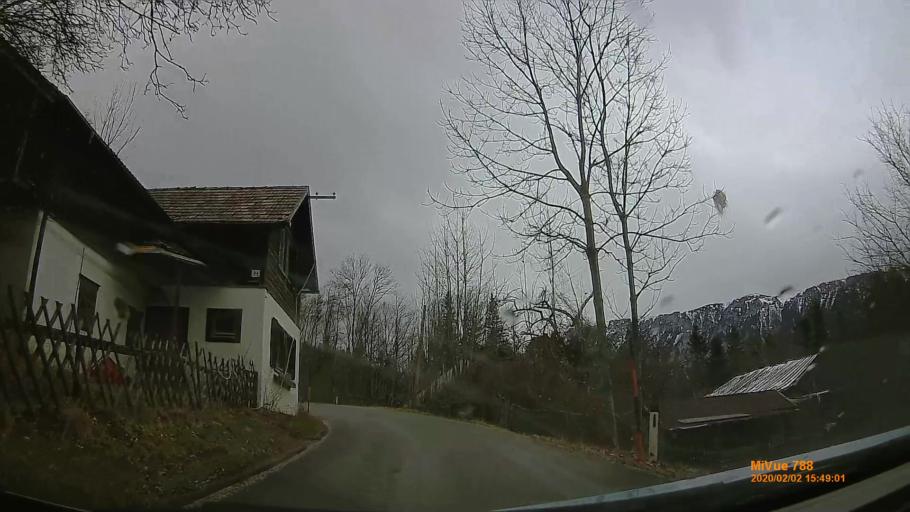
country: AT
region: Lower Austria
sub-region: Politischer Bezirk Neunkirchen
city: Reichenau an der Rax
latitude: 47.6849
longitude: 15.8189
